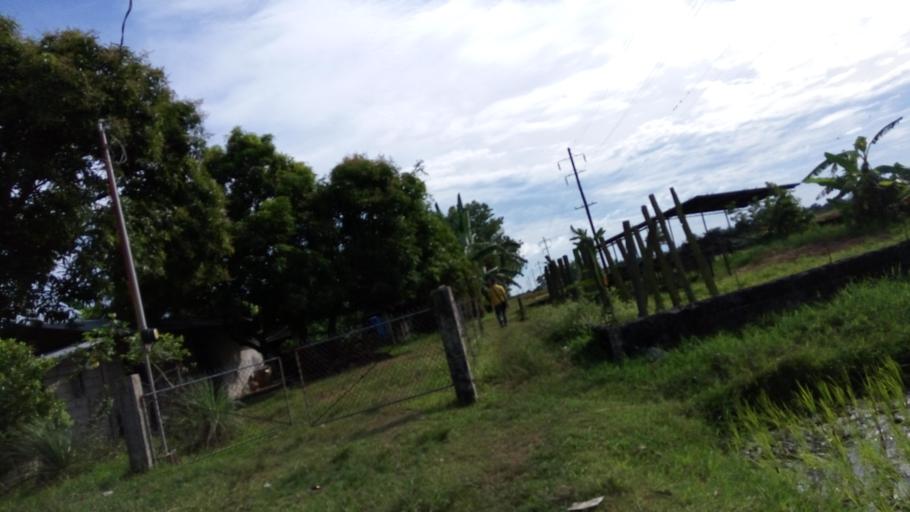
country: PH
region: Ilocos
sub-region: Province of La Union
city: San Eugenio
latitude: 16.3460
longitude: 120.3528
